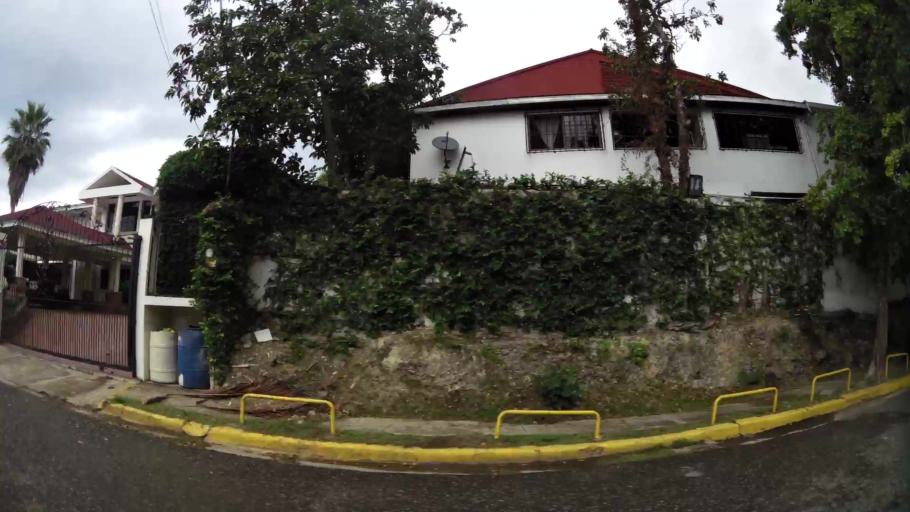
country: DO
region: Nacional
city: La Agustina
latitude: 18.5093
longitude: -69.9428
